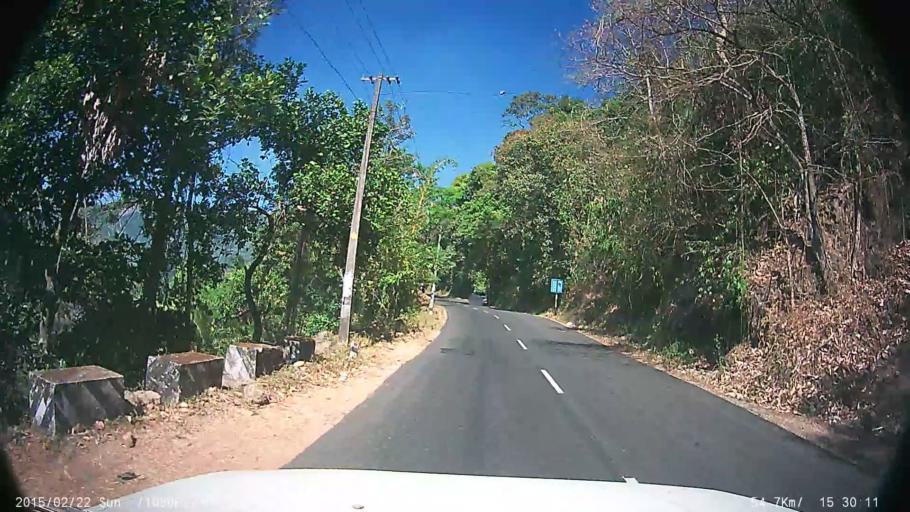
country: IN
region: Kerala
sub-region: Kottayam
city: Erattupetta
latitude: 9.5589
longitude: 76.9523
